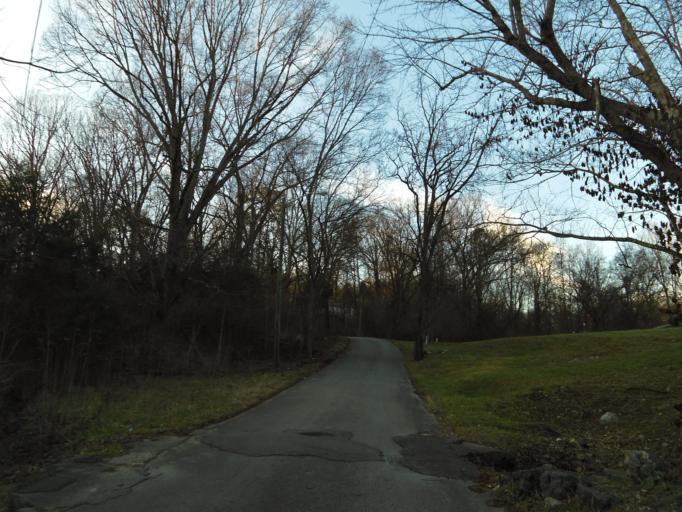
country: US
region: Tennessee
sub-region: Knox County
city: Knoxville
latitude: 36.0153
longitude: -83.8694
